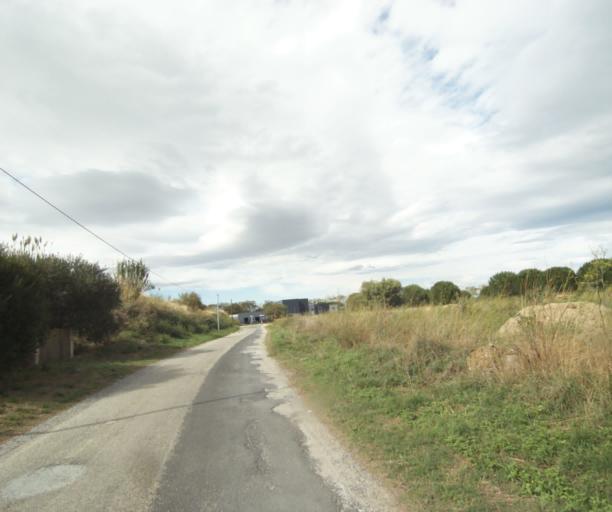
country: FR
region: Languedoc-Roussillon
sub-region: Departement des Pyrenees-Orientales
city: Sant Andreu de Sureda
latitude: 42.5484
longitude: 2.9949
